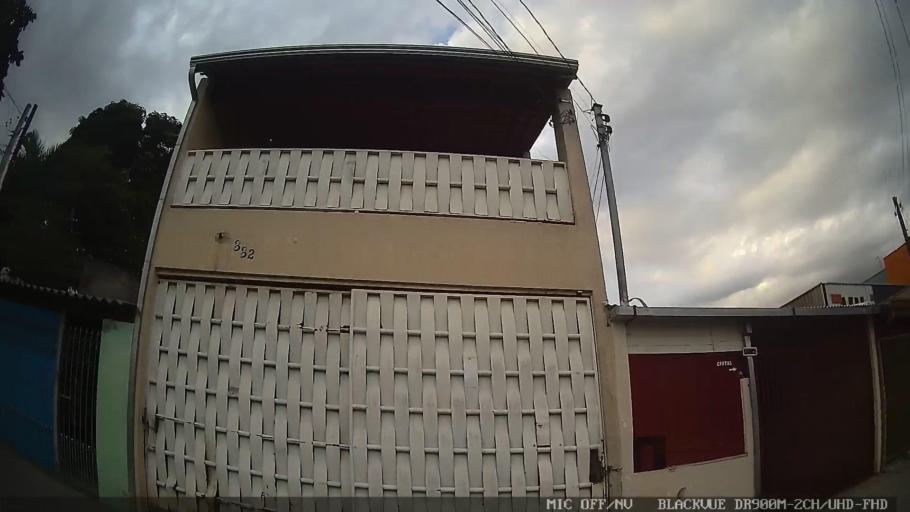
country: BR
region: Sao Paulo
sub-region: Indaiatuba
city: Indaiatuba
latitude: -23.1246
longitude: -47.2421
